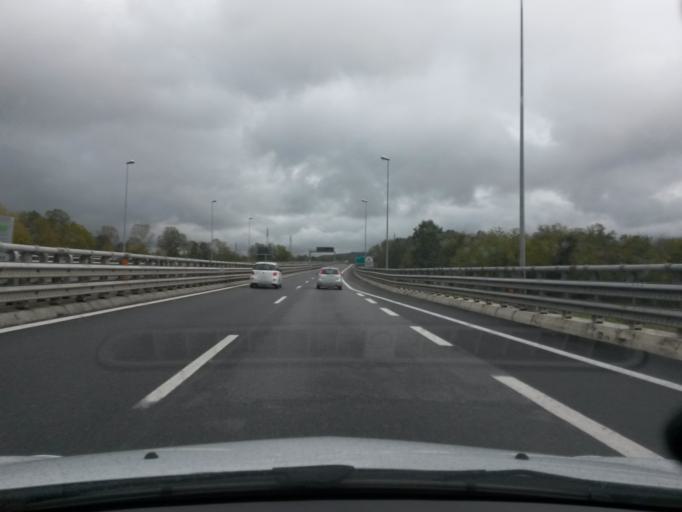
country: IT
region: Piedmont
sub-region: Provincia di Torino
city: Drubiaglio-Grangia
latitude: 45.0910
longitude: 7.4221
